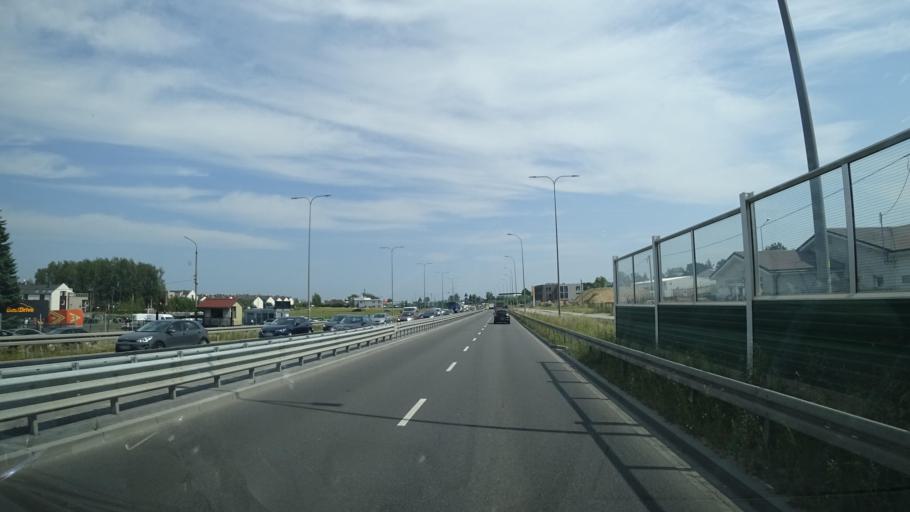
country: PL
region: Pomeranian Voivodeship
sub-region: Powiat gdanski
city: Lublewo Gdanskie
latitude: 54.3512
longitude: 18.5039
